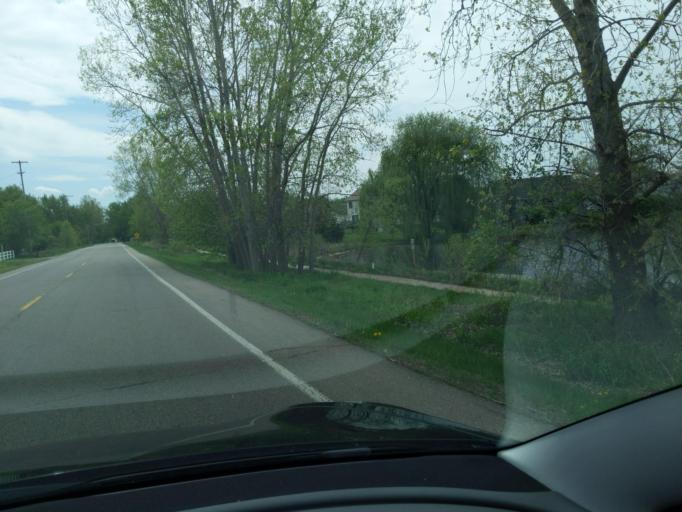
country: US
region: Michigan
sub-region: Ingham County
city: Holt
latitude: 42.6281
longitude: -84.5429
